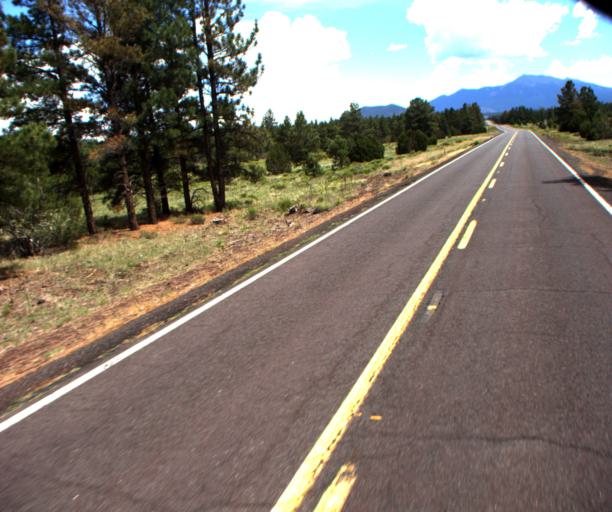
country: US
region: Arizona
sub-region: Coconino County
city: Parks
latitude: 35.4900
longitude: -111.8097
